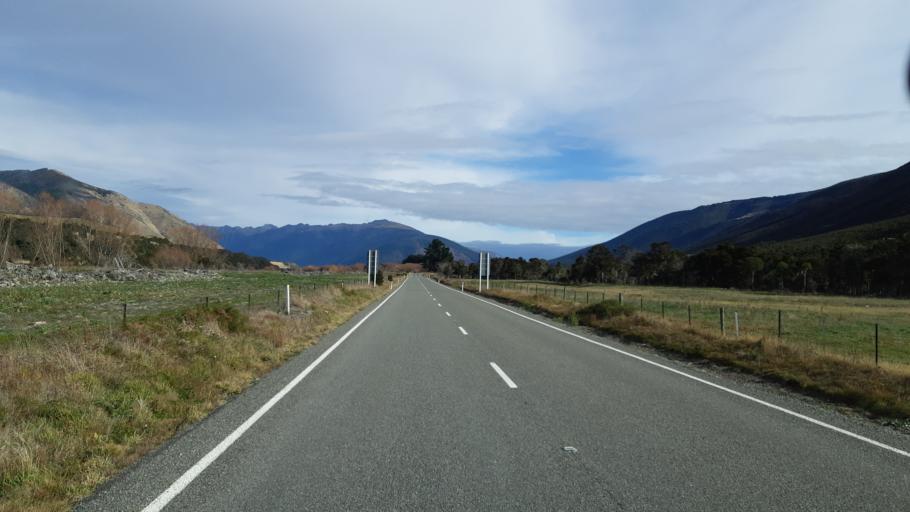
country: NZ
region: Tasman
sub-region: Tasman District
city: Wakefield
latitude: -41.7332
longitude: 173.0298
